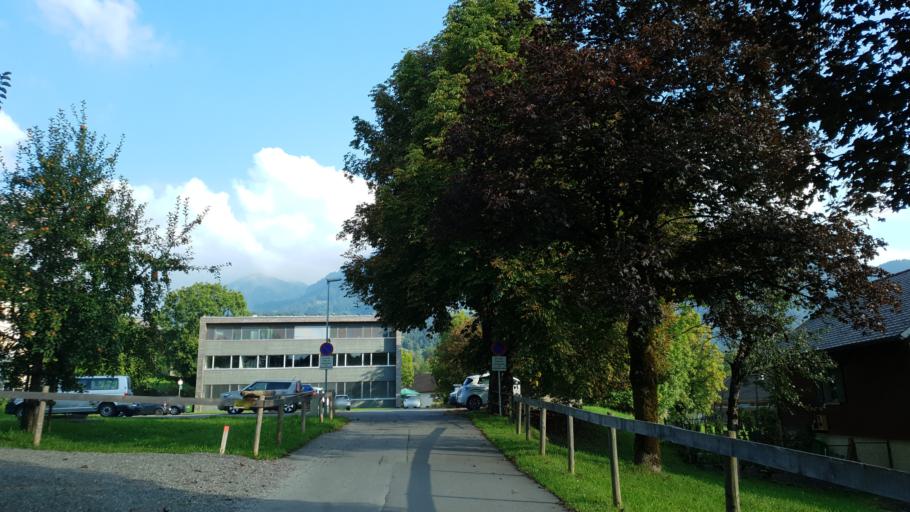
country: AT
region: Vorarlberg
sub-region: Politischer Bezirk Bregenz
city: Egg
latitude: 47.4328
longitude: 9.8984
